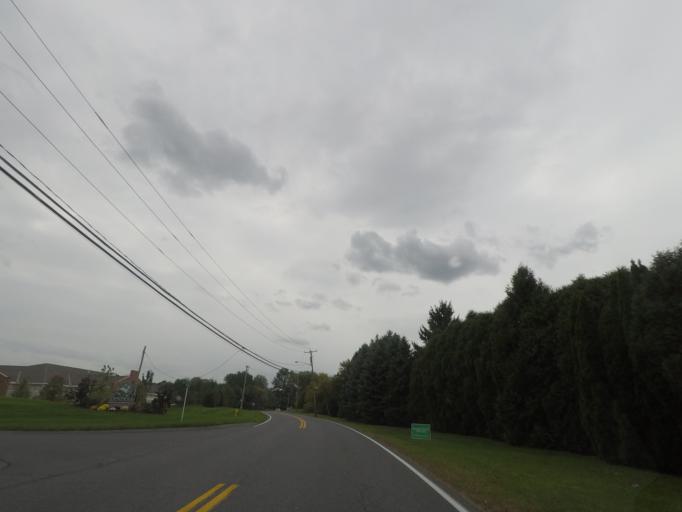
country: US
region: New York
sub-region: Albany County
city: McKownville
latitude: 42.6607
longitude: -73.8351
